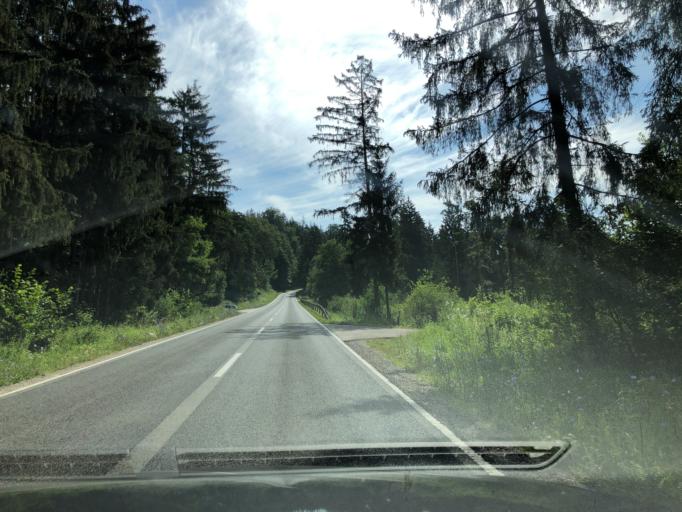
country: DE
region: Bavaria
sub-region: Regierungsbezirk Mittelfranken
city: Greding
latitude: 49.0414
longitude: 11.3777
